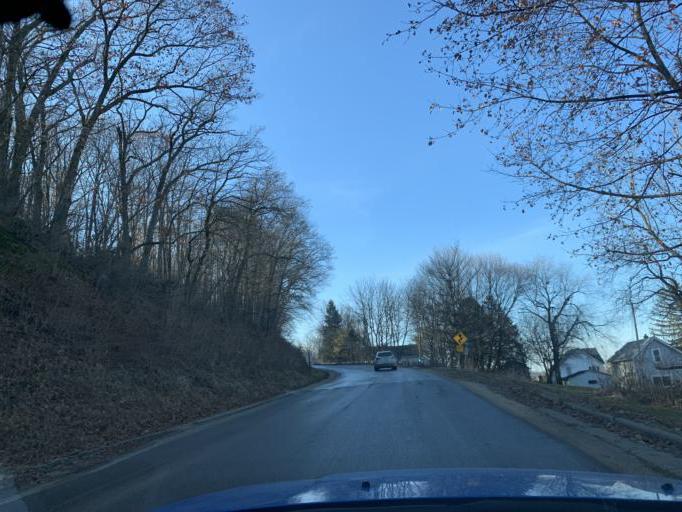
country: US
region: Wisconsin
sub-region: Iowa County
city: Barneveld
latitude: 42.8080
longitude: -89.8634
